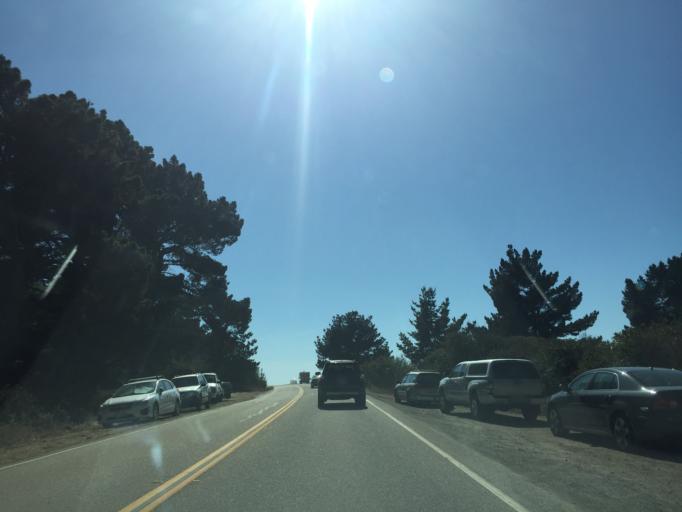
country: US
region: California
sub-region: Monterey County
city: King City
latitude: 35.9179
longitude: -121.4684
